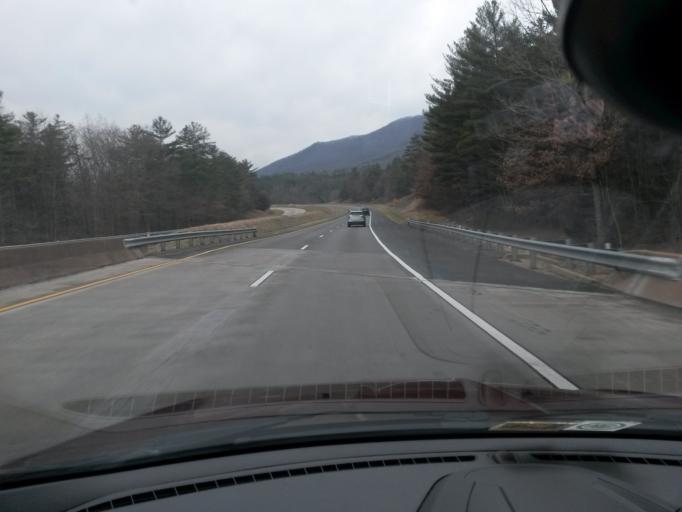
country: US
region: Virginia
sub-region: Alleghany County
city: Clifton Forge
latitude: 37.8135
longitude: -79.6763
